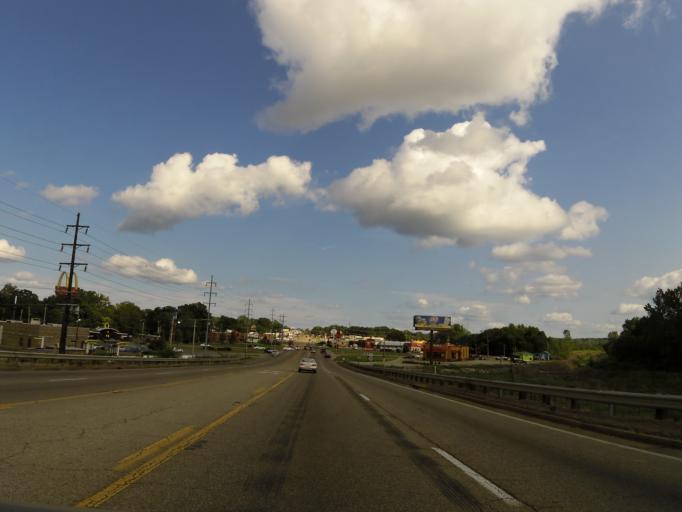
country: US
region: Mississippi
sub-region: Alcorn County
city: Corinth
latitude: 34.9225
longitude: -88.5180
